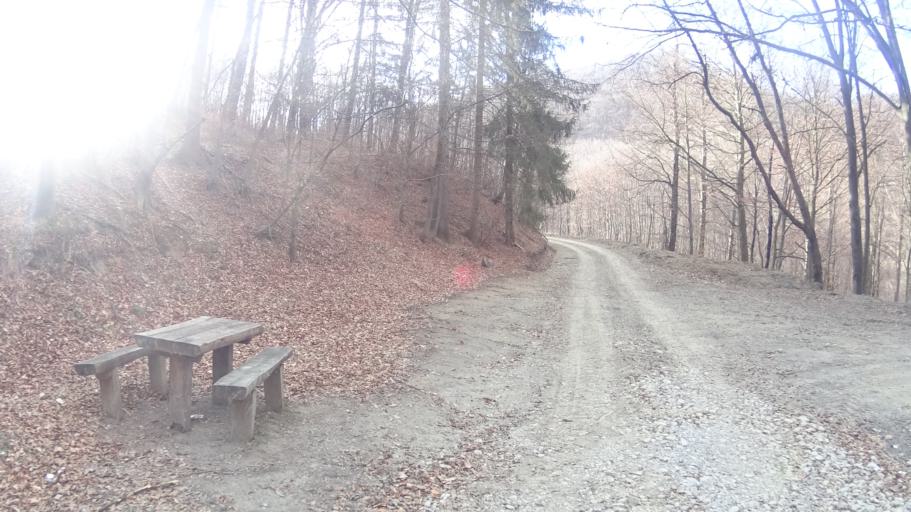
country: HU
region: Heves
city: Szilvasvarad
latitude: 48.0691
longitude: 20.4084
